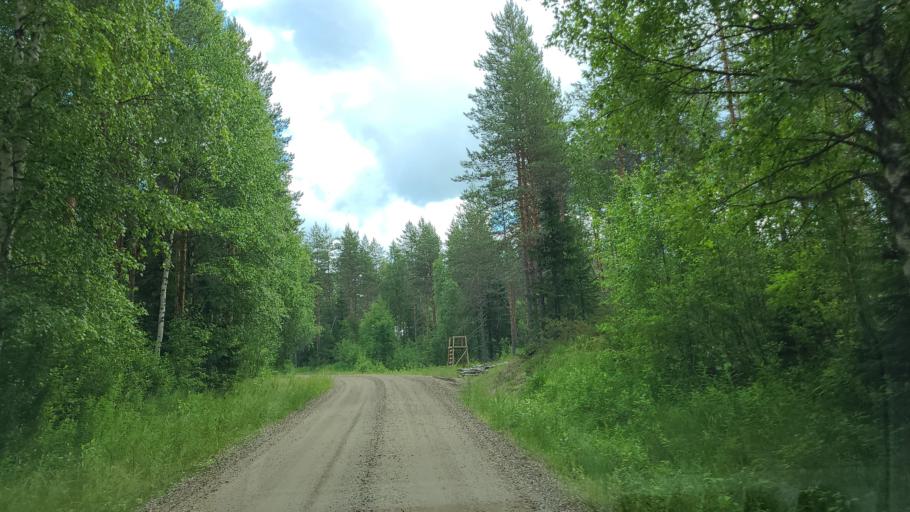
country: FI
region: Northern Savo
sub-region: Koillis-Savo
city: Kaavi
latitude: 63.0355
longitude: 28.7938
